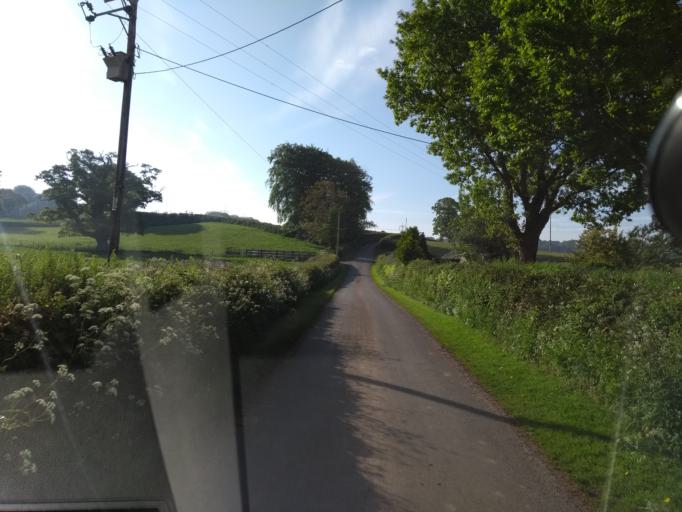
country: GB
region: England
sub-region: Devon
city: Axminster
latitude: 50.7935
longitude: -2.9428
